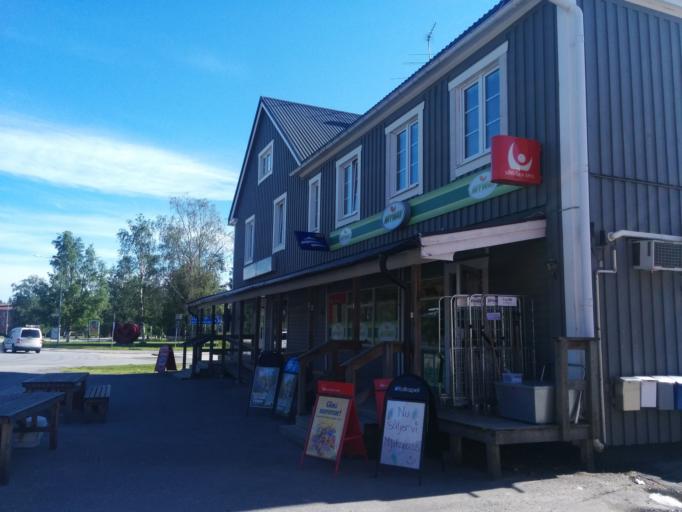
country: SE
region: Vaesterbotten
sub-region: Umea Kommun
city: Hoernefors
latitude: 63.6235
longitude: 19.9081
